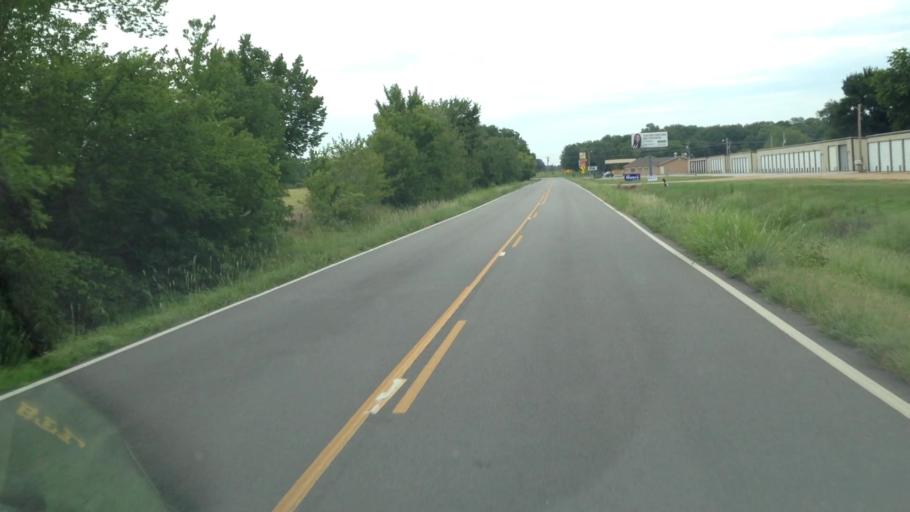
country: US
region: Oklahoma
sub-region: Delaware County
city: Cleora
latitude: 36.5700
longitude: -94.9737
